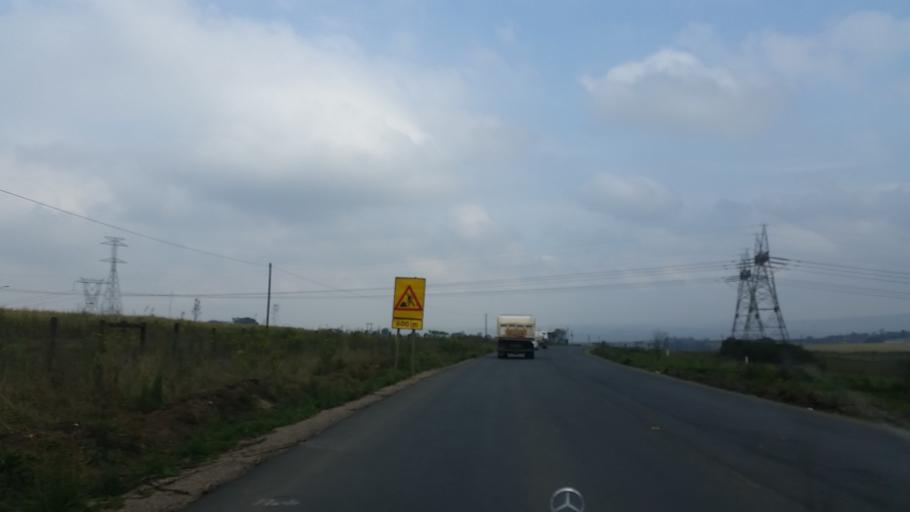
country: ZA
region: KwaZulu-Natal
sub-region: uMgungundlovu District Municipality
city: Camperdown
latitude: -29.7658
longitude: 30.5081
